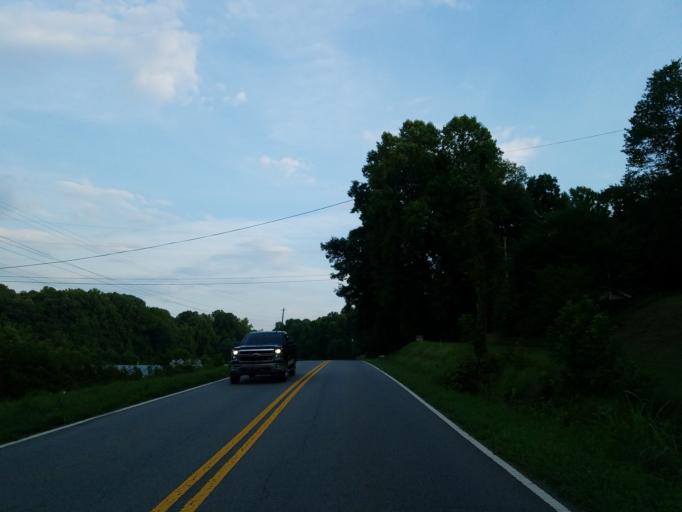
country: US
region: Georgia
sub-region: Gilmer County
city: Ellijay
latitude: 34.6365
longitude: -84.4708
